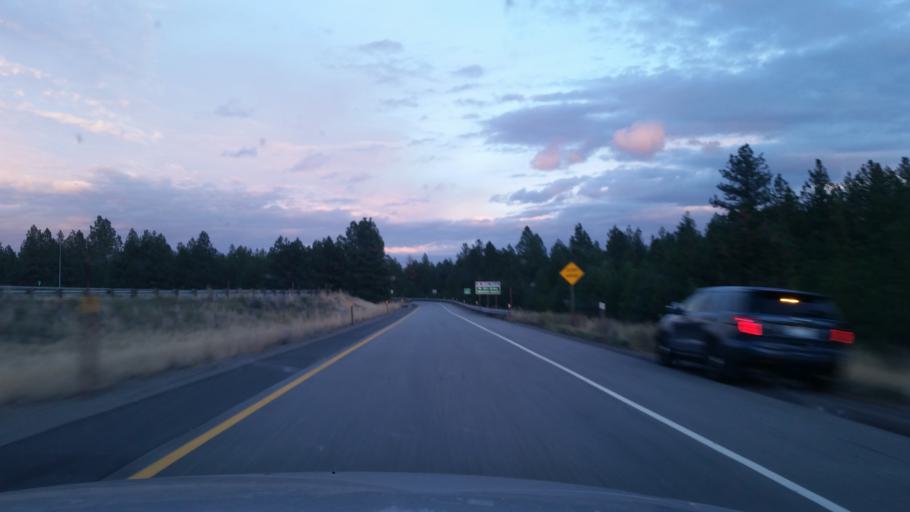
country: US
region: Washington
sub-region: Spokane County
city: Spokane
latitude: 47.6179
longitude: -117.5038
